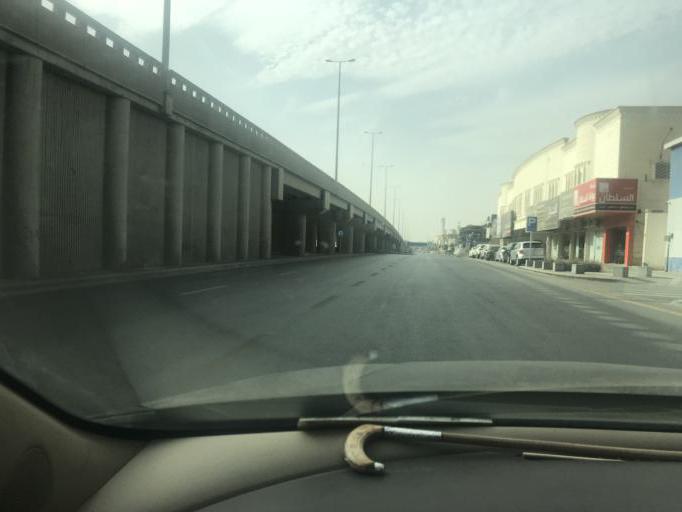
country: SA
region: Ar Riyad
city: Riyadh
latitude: 24.7743
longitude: 46.6665
